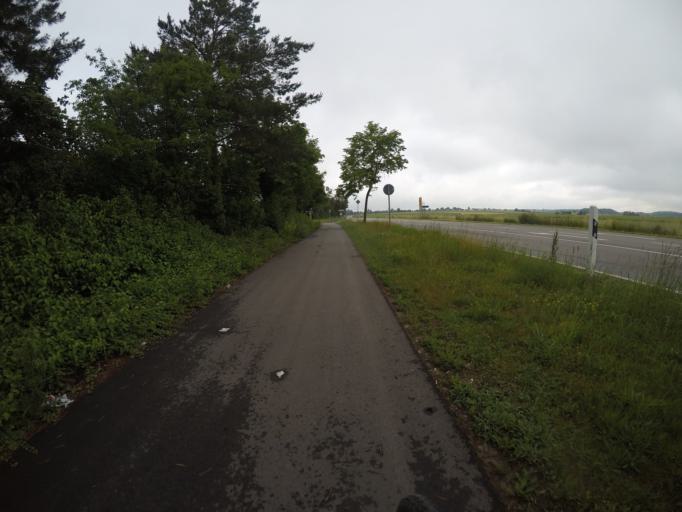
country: DE
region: Baden-Wuerttemberg
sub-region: Tuebingen Region
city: Ulm
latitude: 48.4323
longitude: 9.9857
